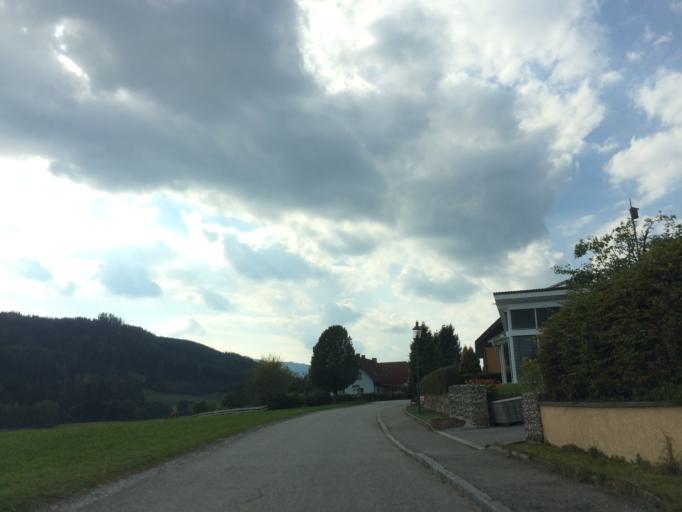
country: AT
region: Styria
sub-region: Politischer Bezirk Murtal
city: Seckau
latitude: 47.2696
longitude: 14.7778
